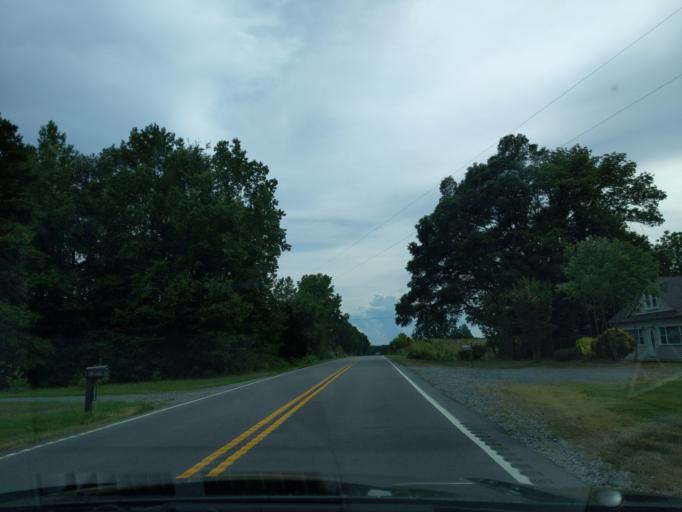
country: US
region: North Carolina
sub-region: Cabarrus County
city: Mount Pleasant
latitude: 35.4494
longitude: -80.3516
